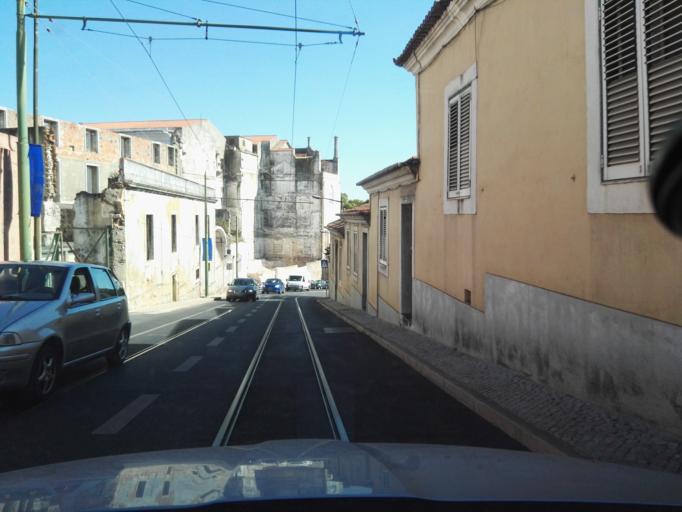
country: PT
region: Lisbon
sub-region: Oeiras
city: Alges
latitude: 38.7082
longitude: -9.1993
